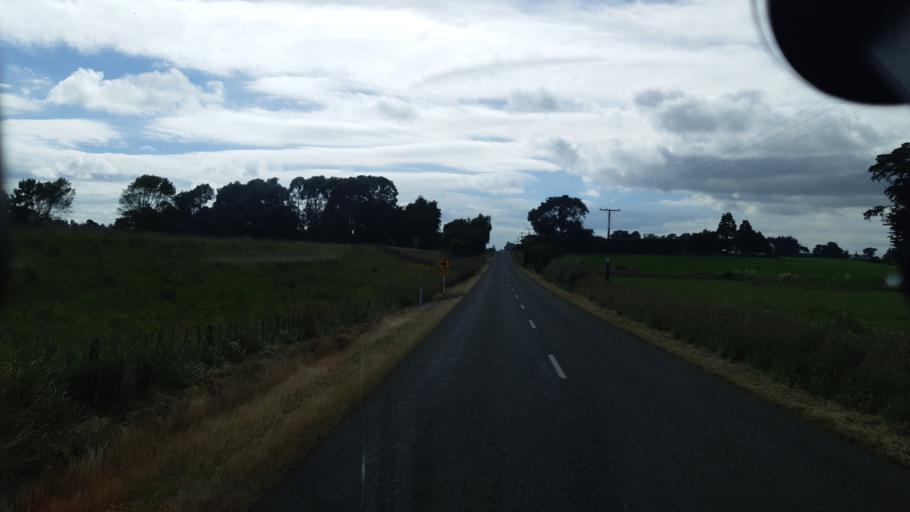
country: NZ
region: Manawatu-Wanganui
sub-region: Rangitikei District
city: Bulls
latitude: -40.0077
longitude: 175.4163
